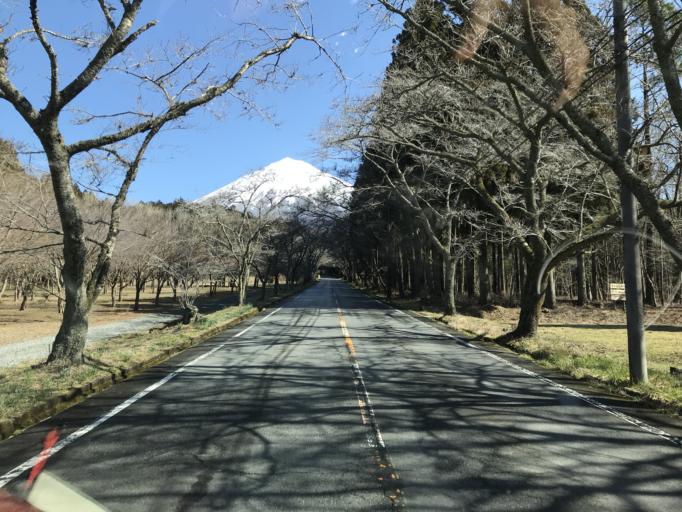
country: JP
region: Shizuoka
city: Fujinomiya
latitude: 35.2796
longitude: 138.6597
